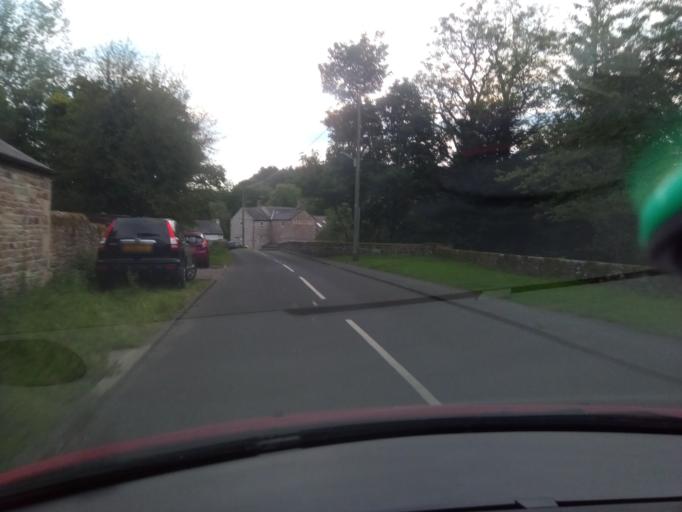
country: GB
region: England
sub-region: Northumberland
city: Bardon Mill
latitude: 54.8981
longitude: -2.2598
